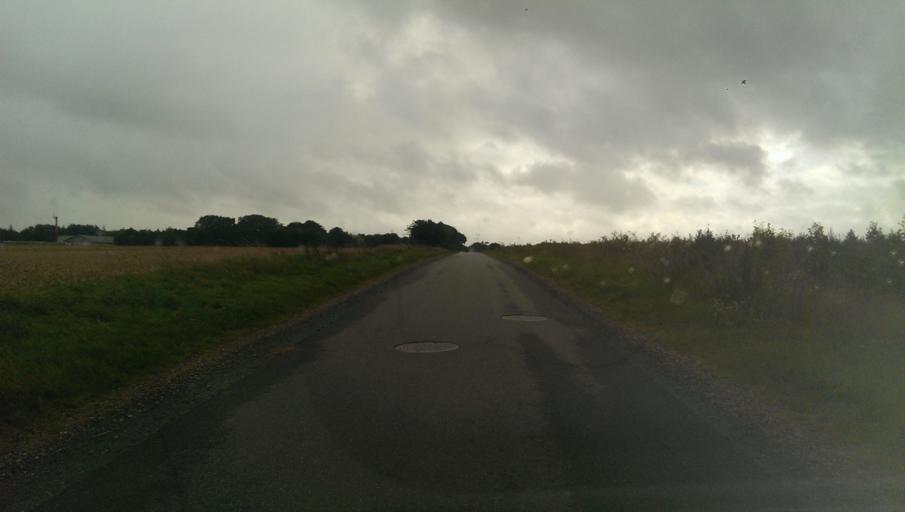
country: DK
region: South Denmark
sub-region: Esbjerg Kommune
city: Tjaereborg
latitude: 55.4680
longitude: 8.5910
